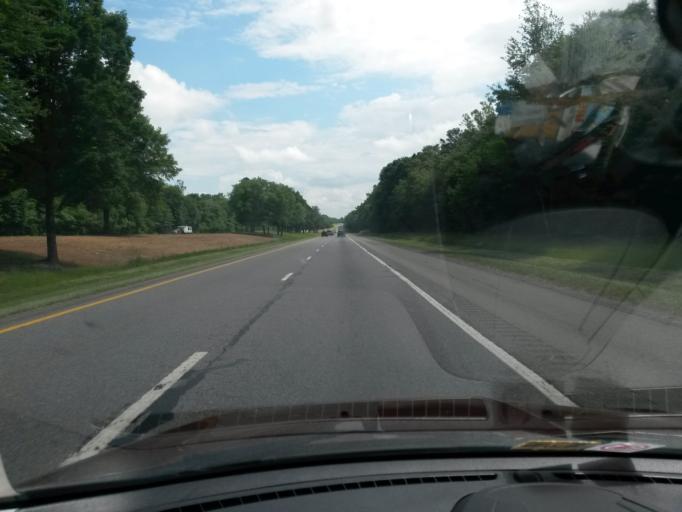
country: US
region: North Carolina
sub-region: Surry County
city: Dobson
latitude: 36.3423
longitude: -80.7950
